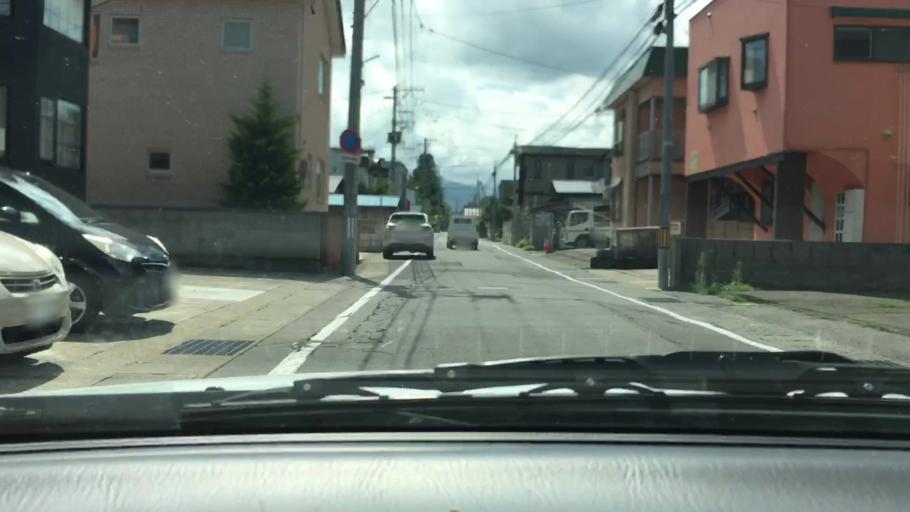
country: JP
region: Aomori
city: Hirosaki
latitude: 40.5918
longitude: 140.4712
